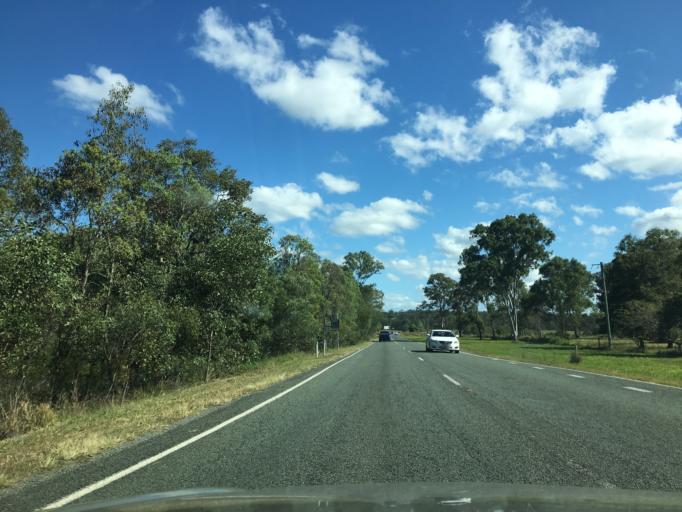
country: AU
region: Queensland
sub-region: Logan
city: Logan Reserve
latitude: -27.7459
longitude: 153.1262
